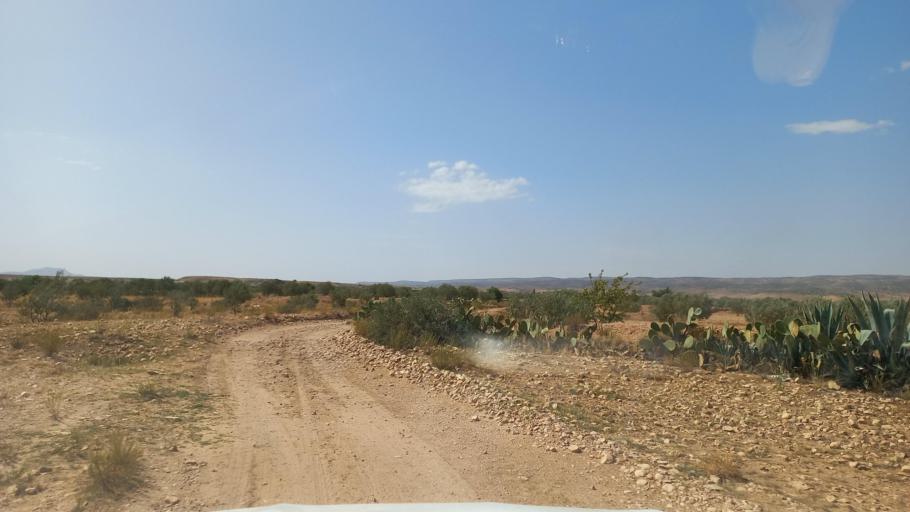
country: TN
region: Al Qasrayn
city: Kasserine
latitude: 35.2579
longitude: 8.9530
